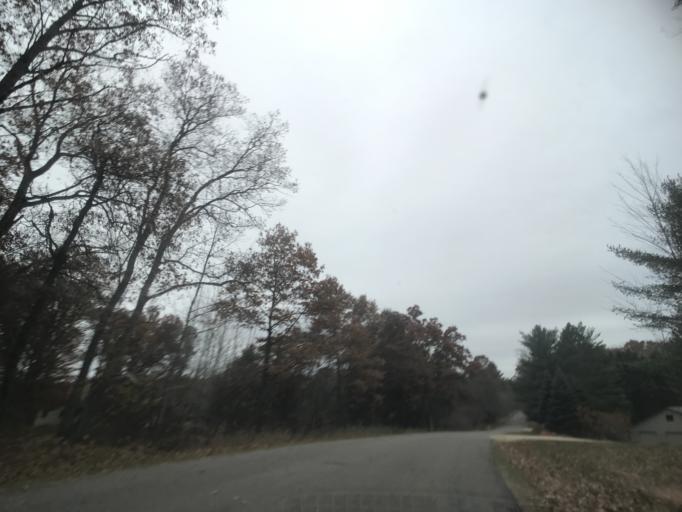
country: US
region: Michigan
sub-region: Dickinson County
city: Kingsford
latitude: 45.3821
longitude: -88.3210
